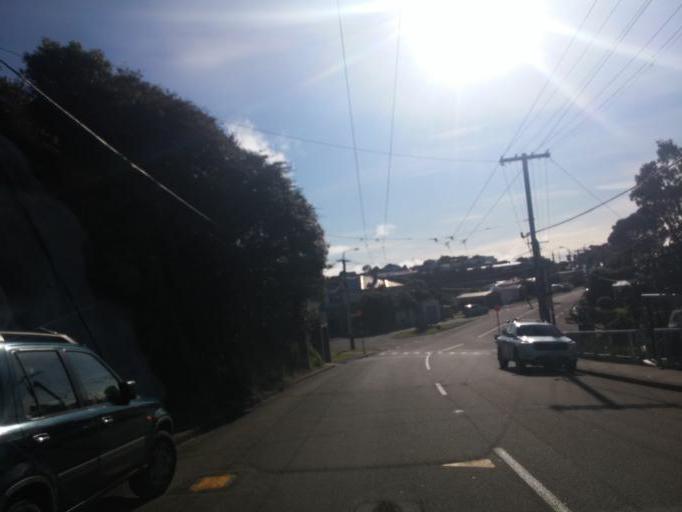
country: NZ
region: Wellington
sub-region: Wellington City
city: Brooklyn
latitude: -41.3185
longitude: 174.7639
